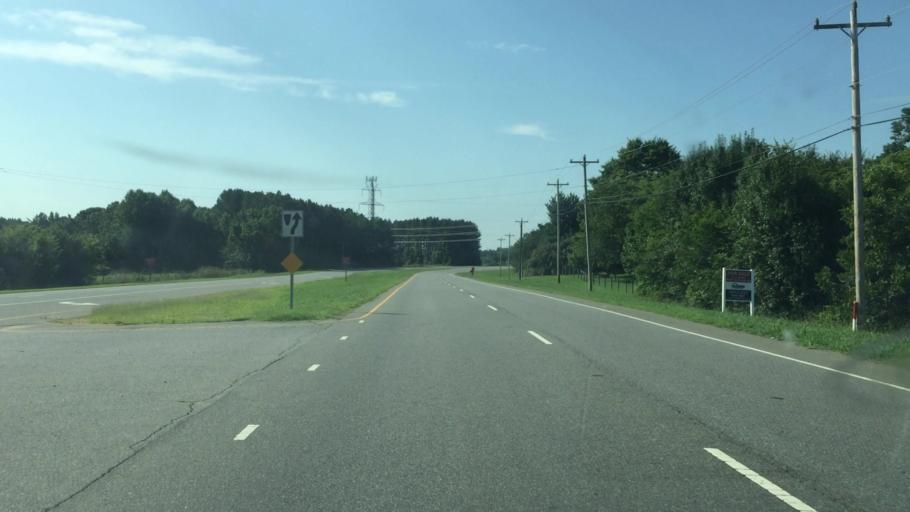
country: US
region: North Carolina
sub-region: Cabarrus County
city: Kannapolis
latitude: 35.4744
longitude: -80.6718
